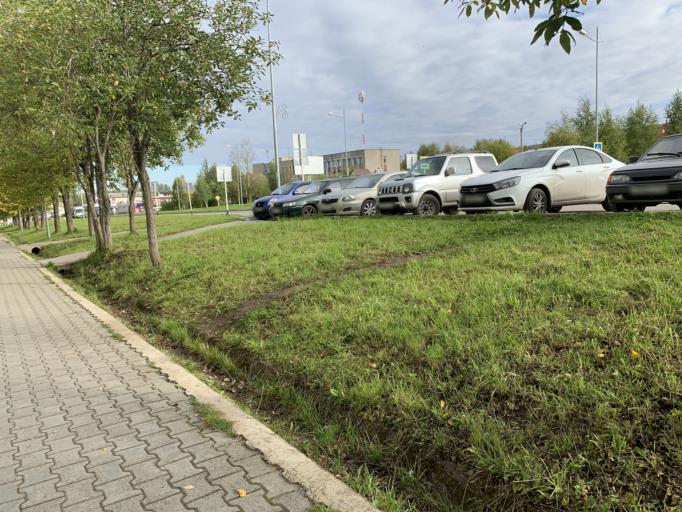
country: RU
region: Perm
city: Gubakha
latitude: 58.8338
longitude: 57.5563
